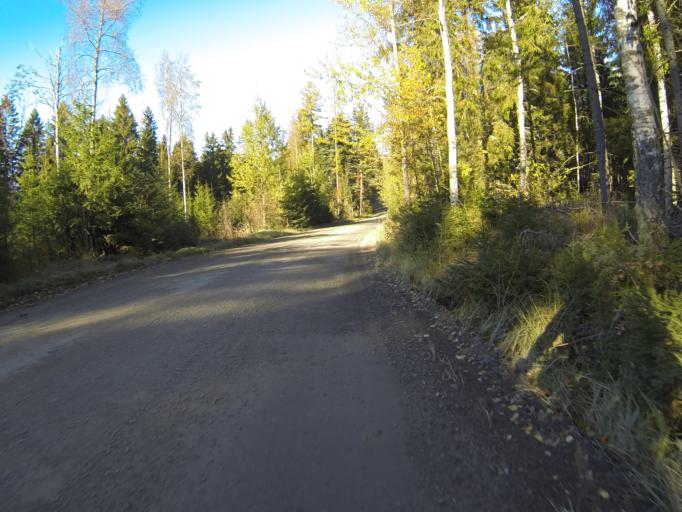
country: FI
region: Varsinais-Suomi
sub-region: Salo
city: Saerkisalo
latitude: 60.2170
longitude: 22.9896
